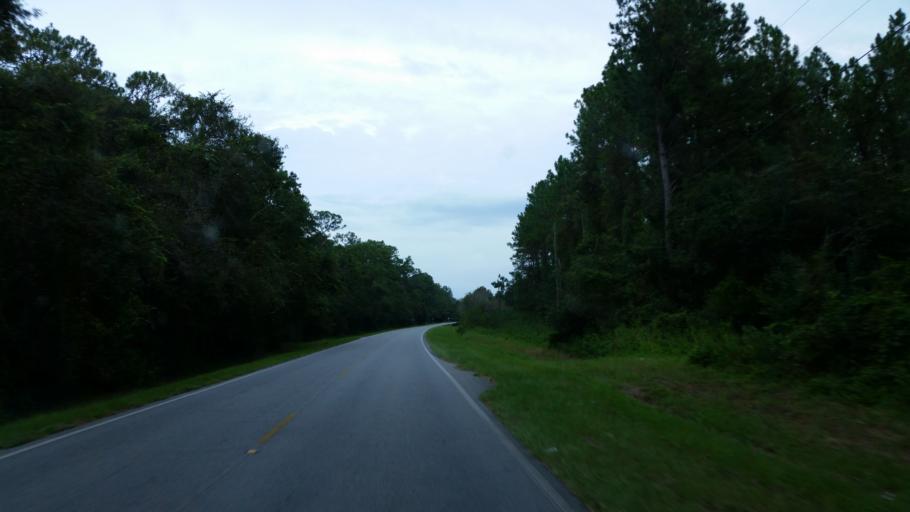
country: US
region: Georgia
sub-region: Lowndes County
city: Valdosta
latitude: 30.7535
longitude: -83.2560
